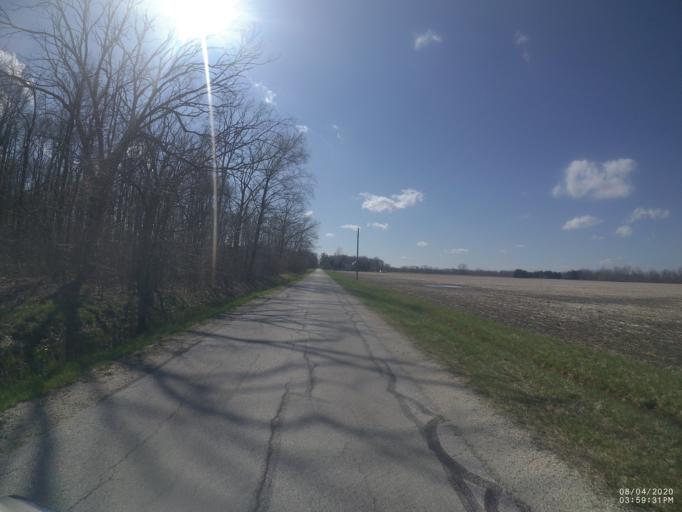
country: US
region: Ohio
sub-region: Sandusky County
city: Ballville
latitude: 41.2619
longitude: -83.1917
